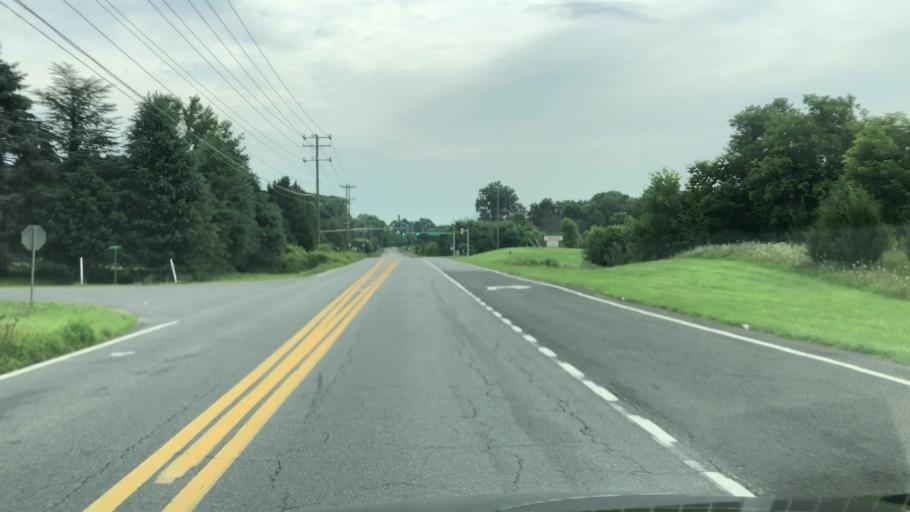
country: US
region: Virginia
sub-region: Fauquier County
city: New Baltimore
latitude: 38.7342
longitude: -77.6855
